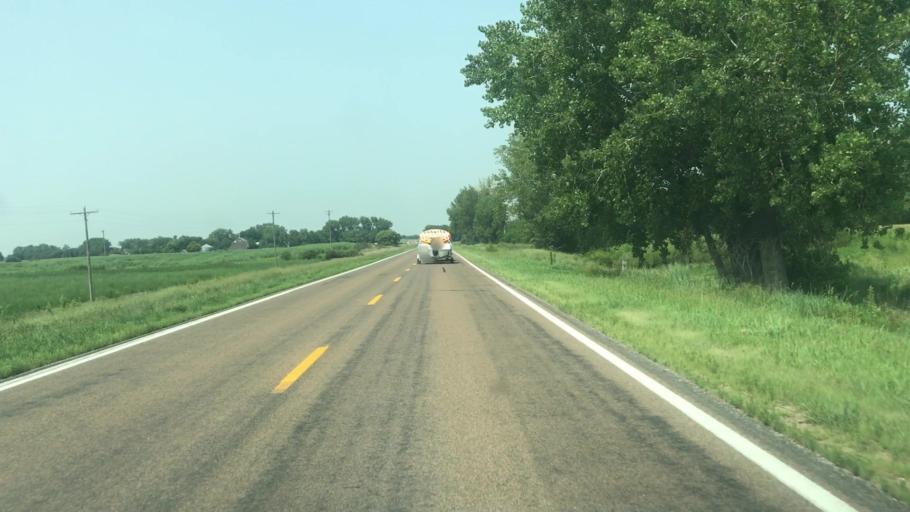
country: US
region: Nebraska
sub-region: Sherman County
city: Loup City
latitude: 41.2409
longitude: -98.9386
